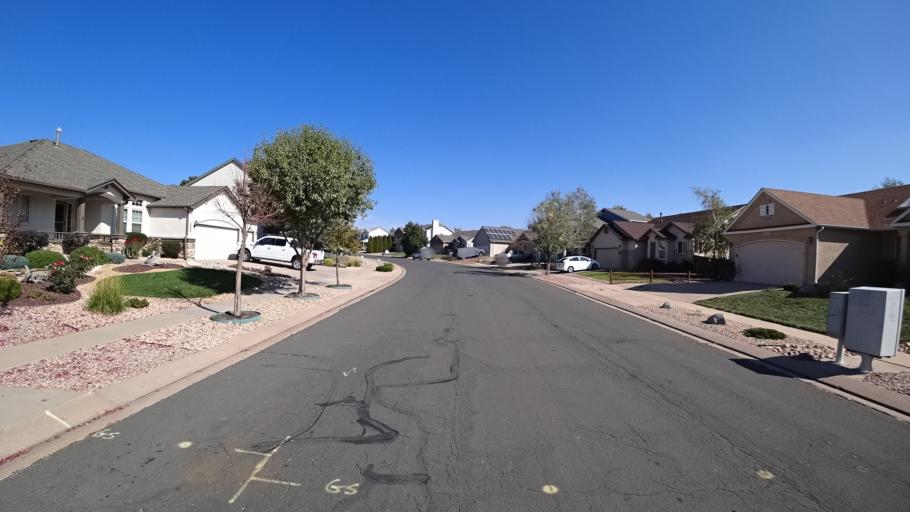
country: US
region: Colorado
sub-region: El Paso County
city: Cimarron Hills
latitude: 38.8807
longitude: -104.7076
